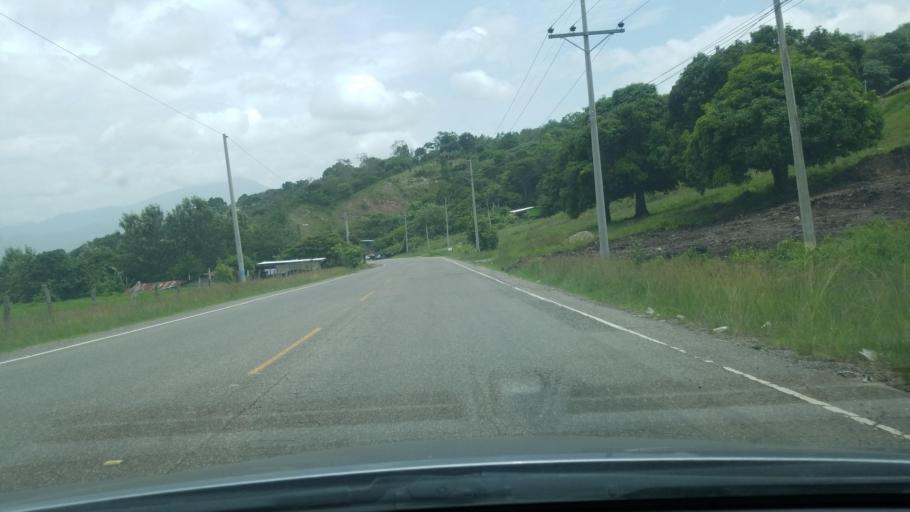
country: HN
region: Copan
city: Ojos de Agua
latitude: 14.6764
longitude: -88.8155
